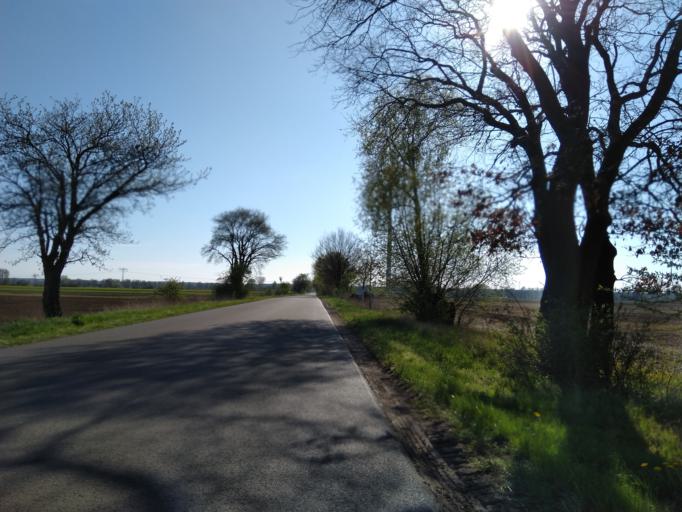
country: DE
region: Brandenburg
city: Bliesdorf
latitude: 52.7007
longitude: 14.1813
